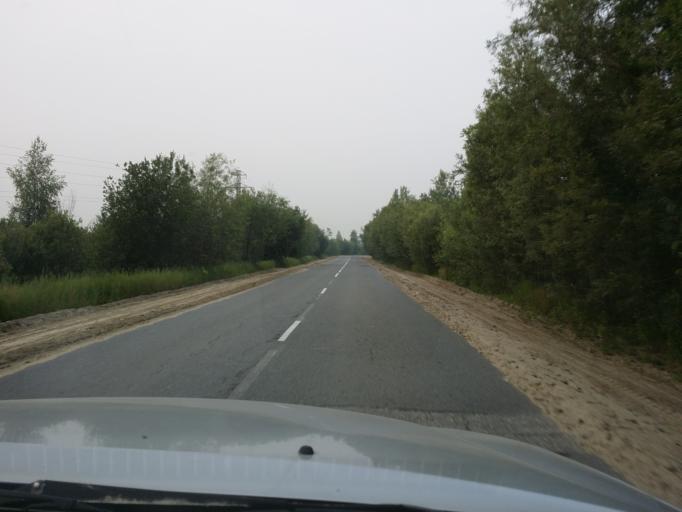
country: RU
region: Khanty-Mansiyskiy Avtonomnyy Okrug
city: Megion
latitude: 60.9953
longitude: 76.3014
